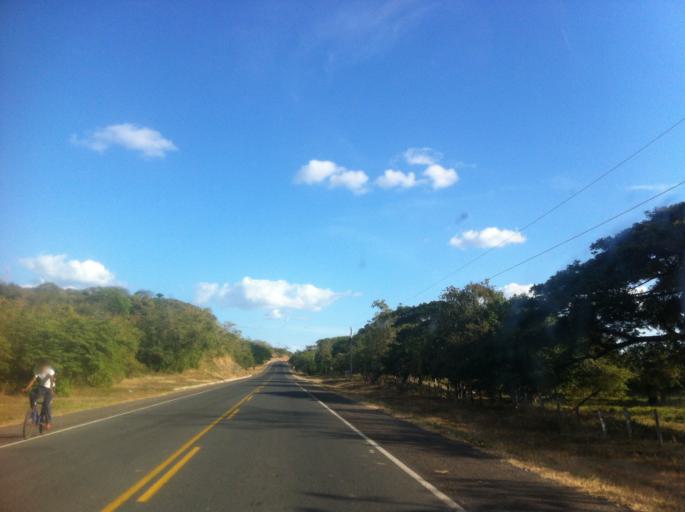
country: NI
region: Chontales
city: Acoyapa
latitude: 11.9503
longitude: -85.1553
